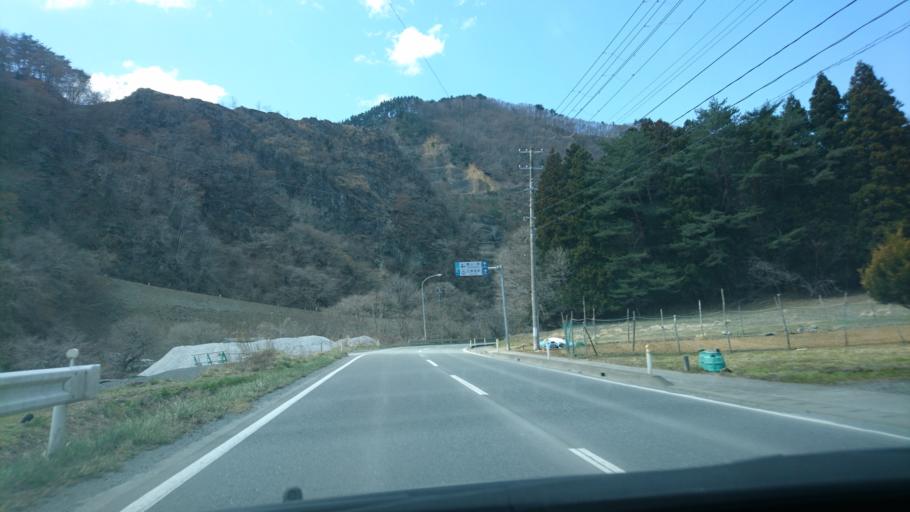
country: JP
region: Iwate
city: Ofunato
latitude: 39.1210
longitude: 141.6729
